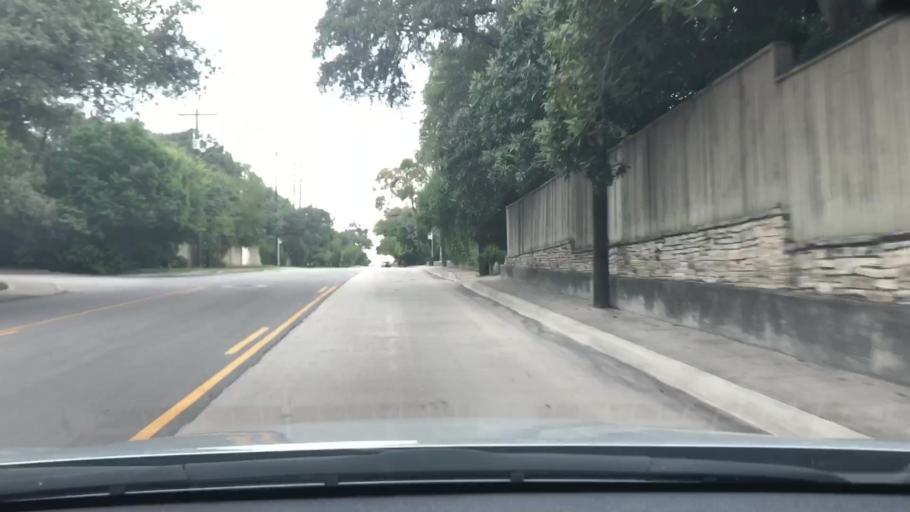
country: US
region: Texas
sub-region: Bexar County
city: Alamo Heights
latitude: 29.5109
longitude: -98.4555
